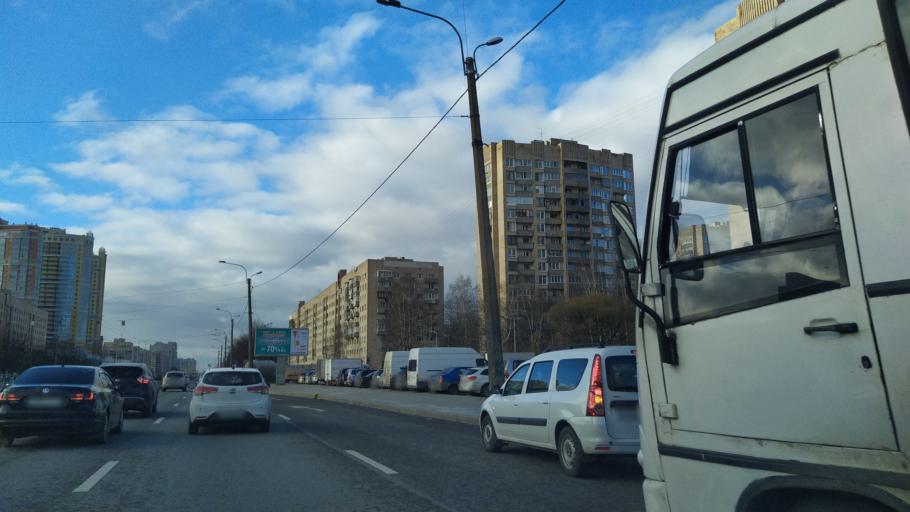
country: RU
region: Leningrad
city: Bugry
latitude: 60.0452
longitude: 30.3729
